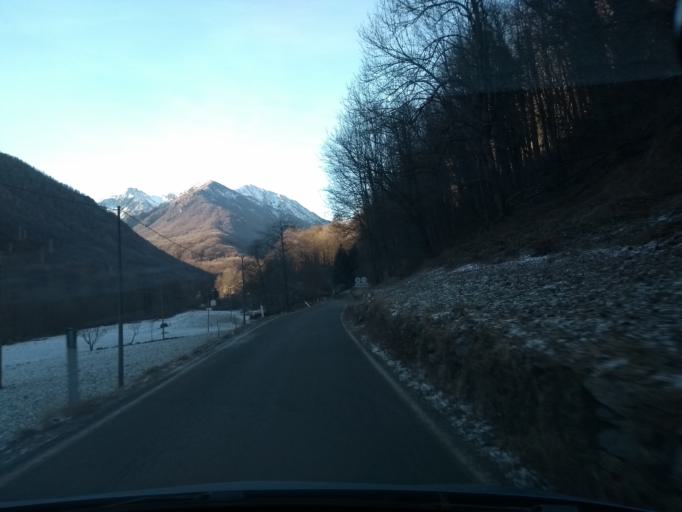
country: IT
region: Piedmont
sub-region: Provincia di Torino
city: Viu
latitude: 45.2285
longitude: 7.3425
